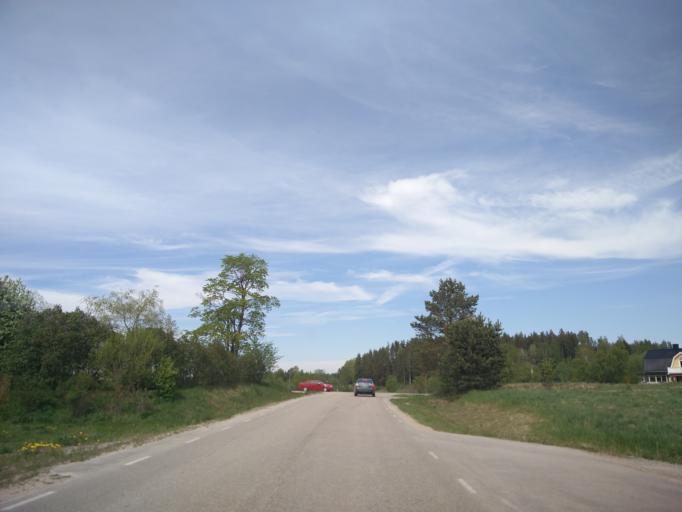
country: SE
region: Gaevleborg
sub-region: Hudiksvalls Kommun
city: Sorforsa
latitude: 61.6983
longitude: 16.9315
